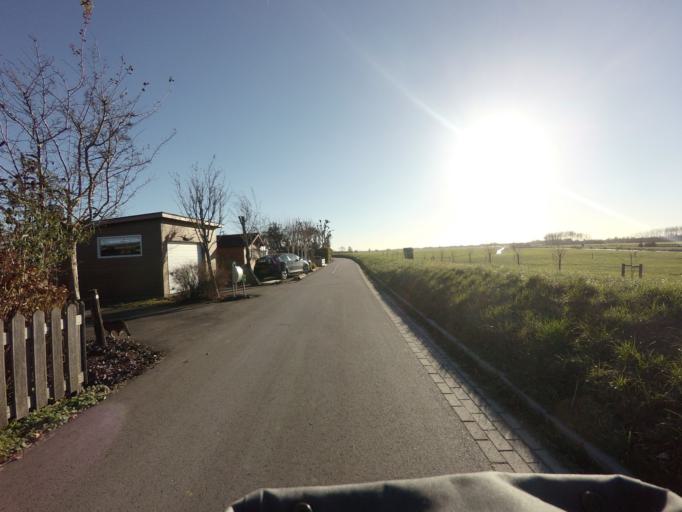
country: NL
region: North Holland
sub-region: Gemeente Amsterdam
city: Amsterdam-Zuidoost
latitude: 52.2613
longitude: 4.9739
